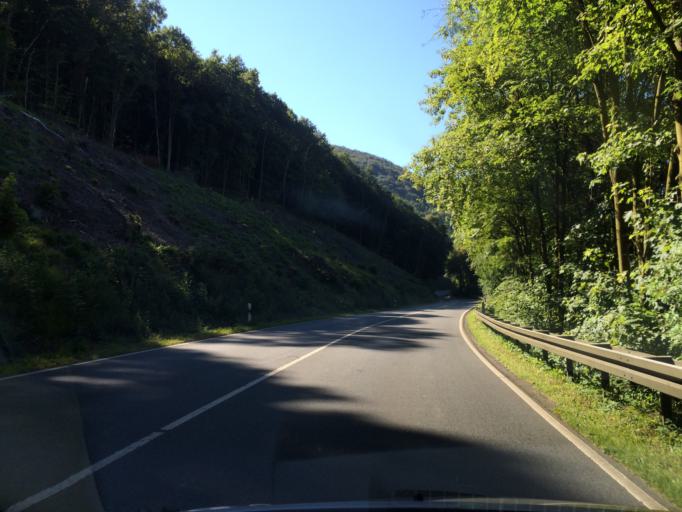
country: DE
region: North Rhine-Westphalia
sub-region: Regierungsbezirk Arnsberg
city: Nachrodt-Wiblingwerde
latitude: 51.3560
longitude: 7.6410
